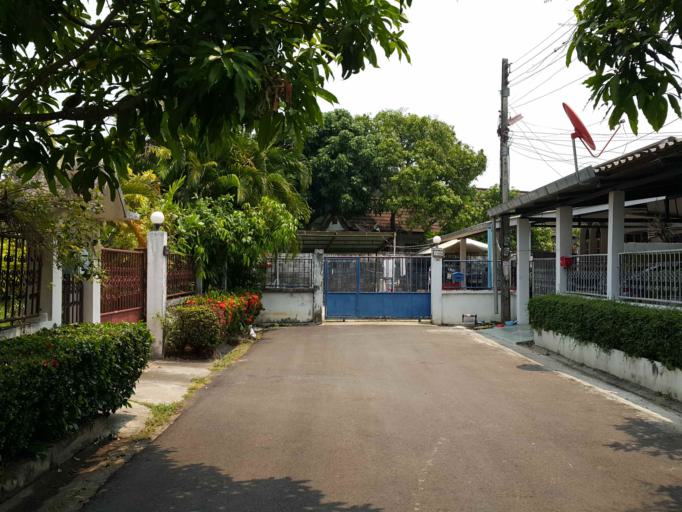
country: TH
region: Chiang Mai
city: Chiang Mai
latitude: 18.7554
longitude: 99.0142
